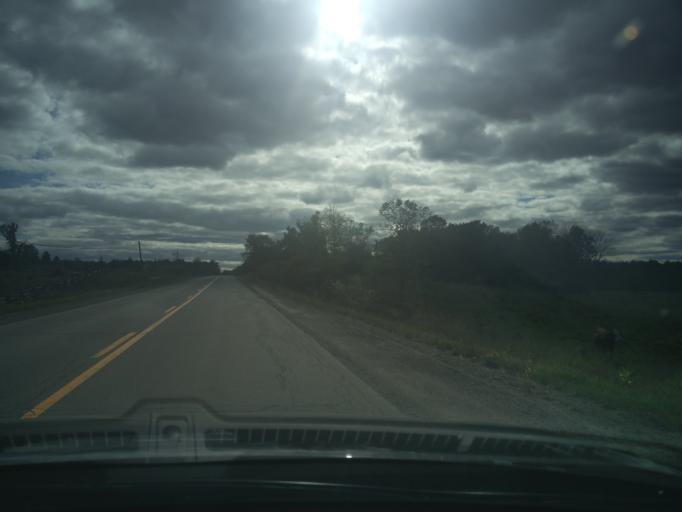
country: CA
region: Ontario
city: Perth
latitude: 44.7282
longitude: -76.3980
